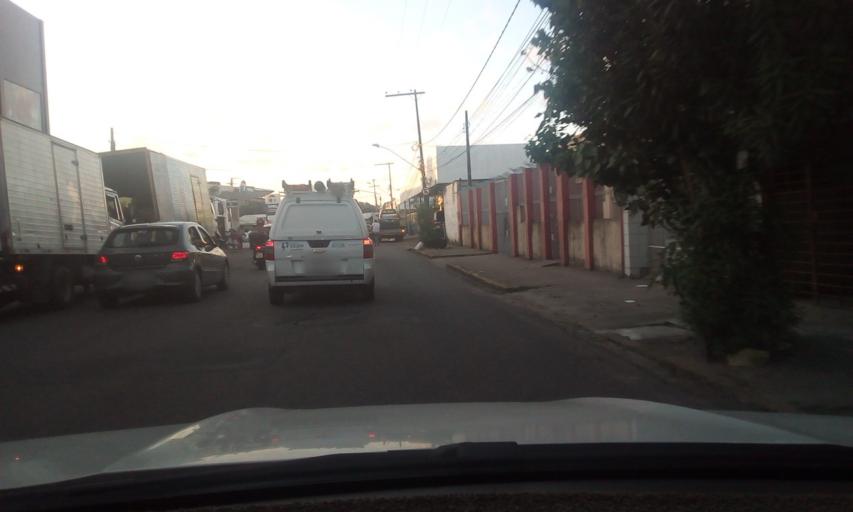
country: BR
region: Pernambuco
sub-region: Recife
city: Recife
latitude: -8.0768
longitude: -34.9066
